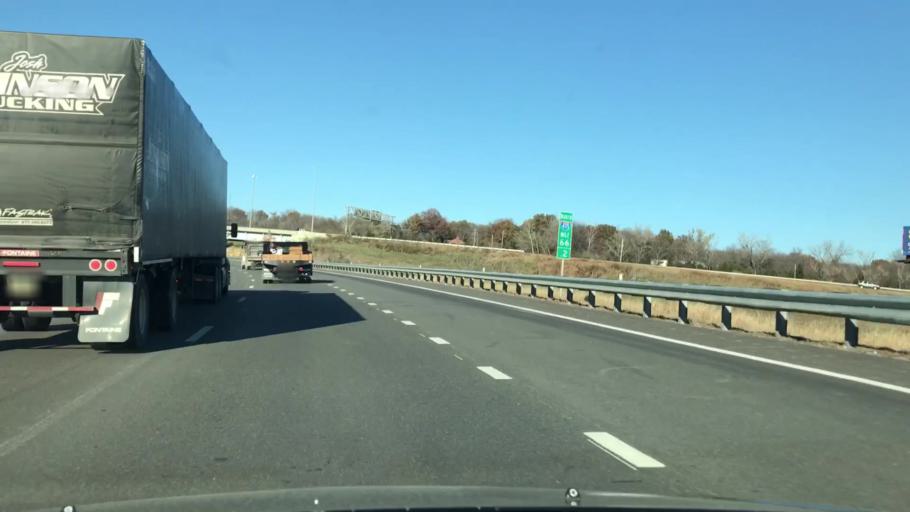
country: US
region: Missouri
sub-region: Jackson County
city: Raytown
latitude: 39.0141
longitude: -94.4970
